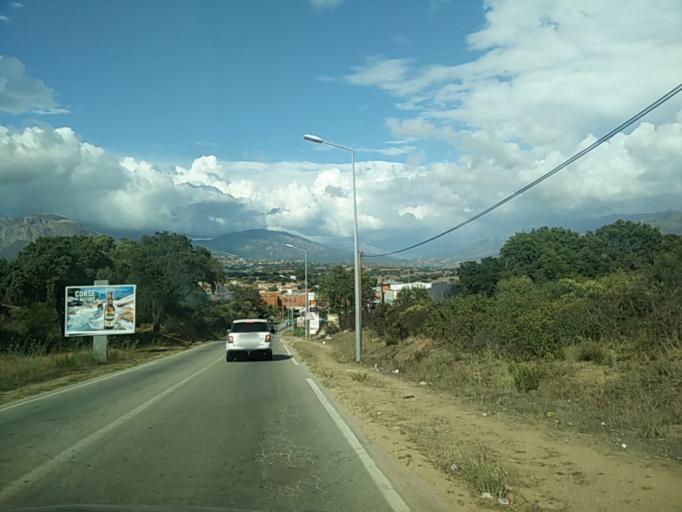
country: FR
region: Corsica
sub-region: Departement de la Corse-du-Sud
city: Afa
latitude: 41.9474
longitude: 8.7734
